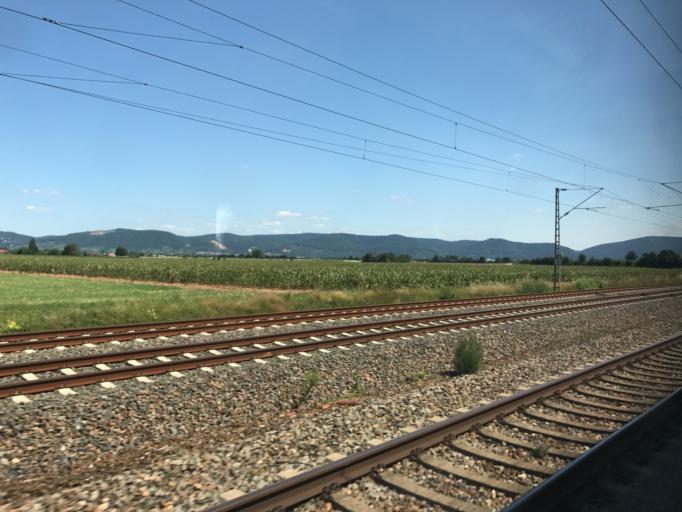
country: DE
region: Baden-Wuerttemberg
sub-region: Karlsruhe Region
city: Edingen-Neckarhausen
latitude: 49.4303
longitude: 8.5932
